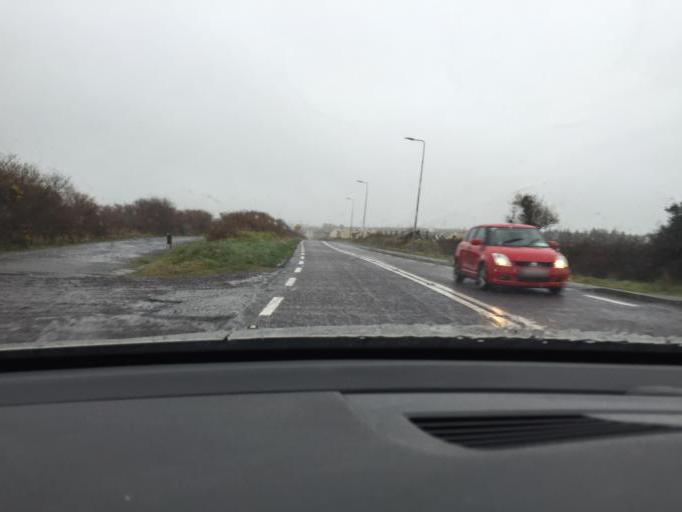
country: IE
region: Munster
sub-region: Ciarrai
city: Dingle
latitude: 52.1439
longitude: -10.1499
